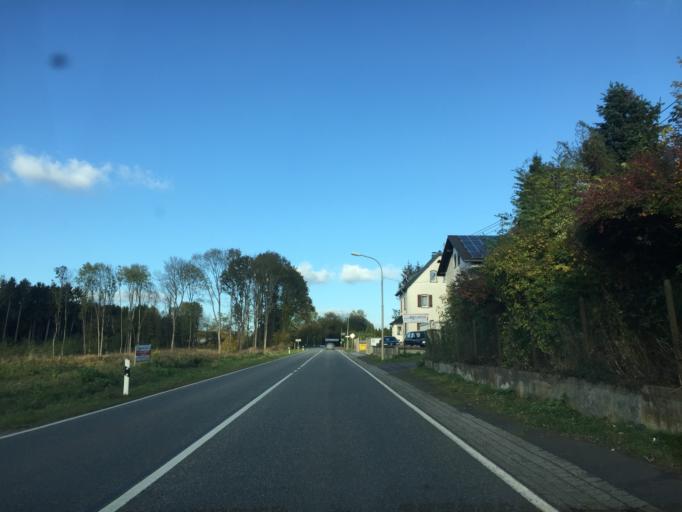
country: DE
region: Rheinland-Pfalz
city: Dreikirchen
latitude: 50.4477
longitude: 7.9427
